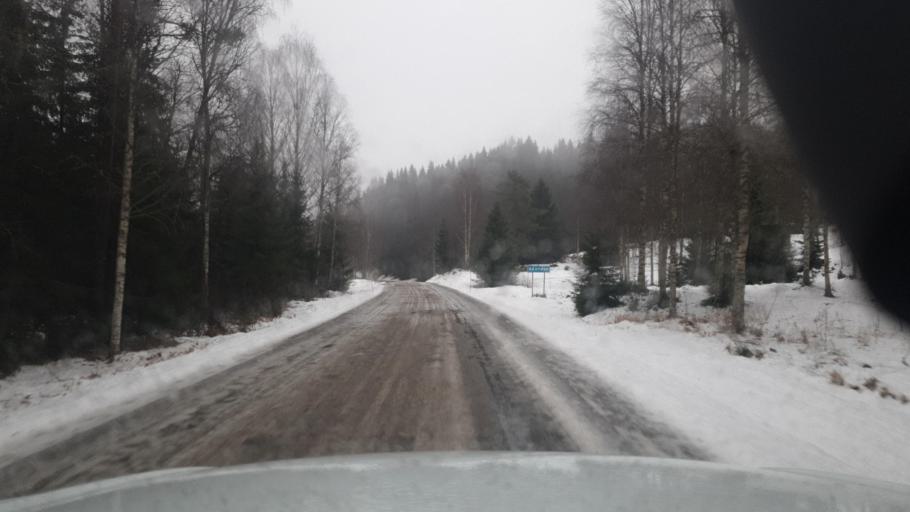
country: SE
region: Vaermland
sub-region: Eda Kommun
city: Charlottenberg
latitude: 60.0160
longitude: 12.6348
